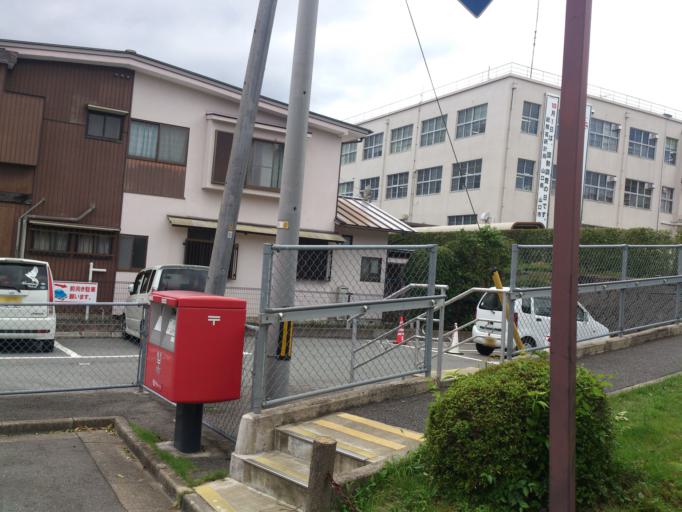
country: JP
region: Yamaguchi
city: Yamaguchi-shi
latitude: 34.1781
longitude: 131.4746
